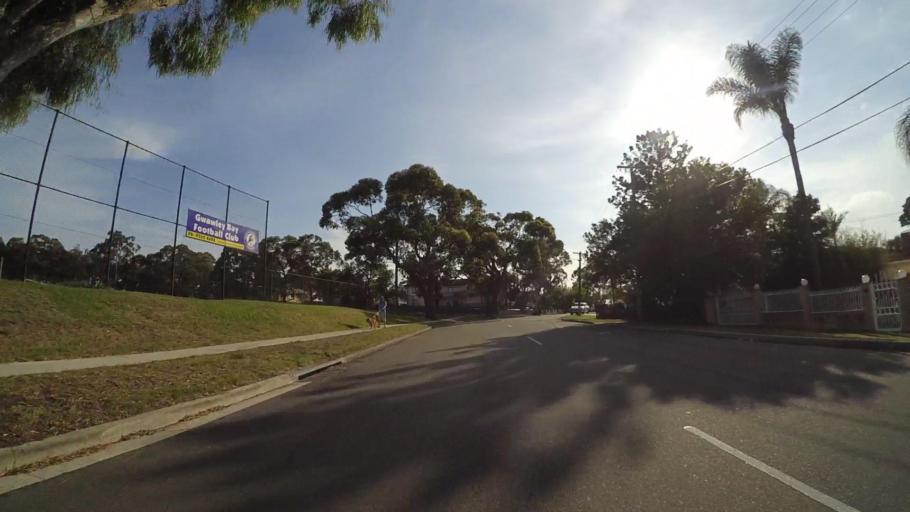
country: AU
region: New South Wales
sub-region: Kogarah
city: Blakehurst
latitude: -34.0124
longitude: 151.1087
